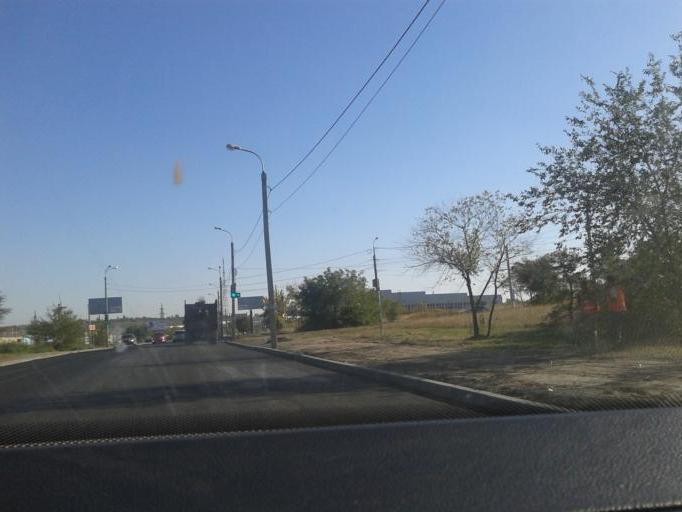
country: RU
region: Volgograd
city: Volgograd
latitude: 48.7589
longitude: 44.5224
